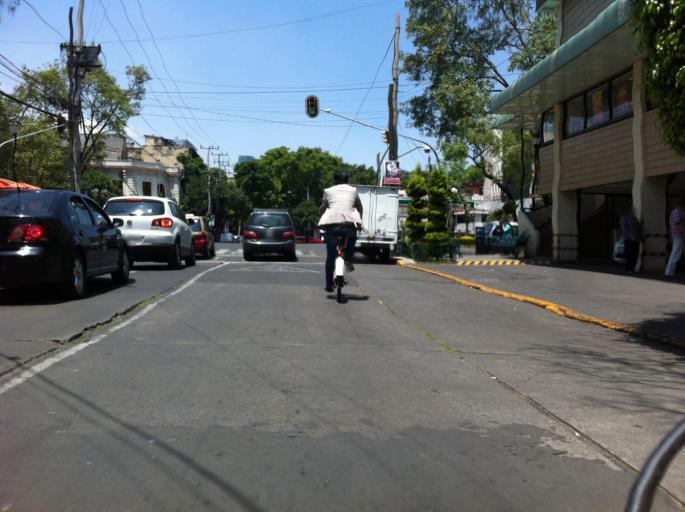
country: MX
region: Mexico City
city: Benito Juarez
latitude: 19.4180
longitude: -99.1573
